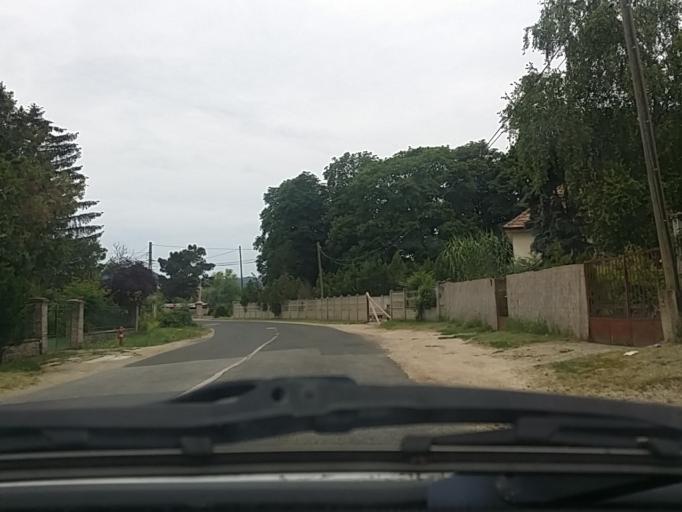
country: HU
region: Pest
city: Pilisvorosvar
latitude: 47.6249
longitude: 18.9154
